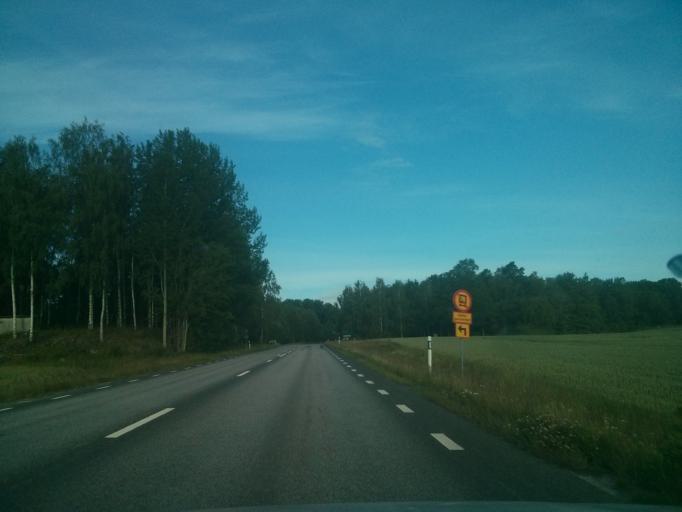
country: SE
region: Soedermanland
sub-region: Katrineholms Kommun
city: Katrineholm
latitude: 58.9676
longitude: 16.3392
